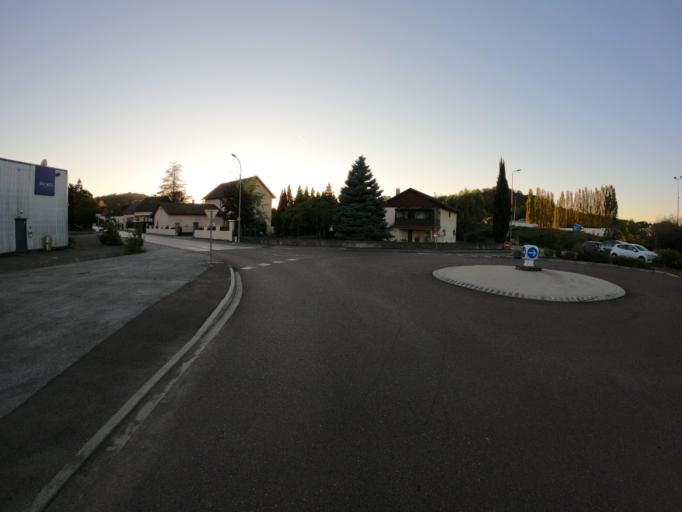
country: FR
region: Franche-Comte
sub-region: Departement du Jura
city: Montmorot
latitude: 46.6754
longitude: 5.5351
